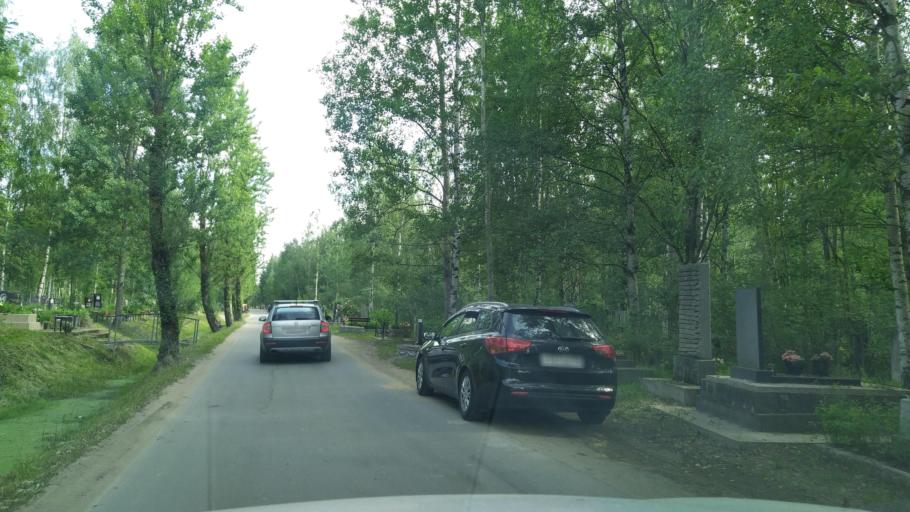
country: RU
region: St.-Petersburg
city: Dachnoye
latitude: 59.7669
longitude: 30.2626
